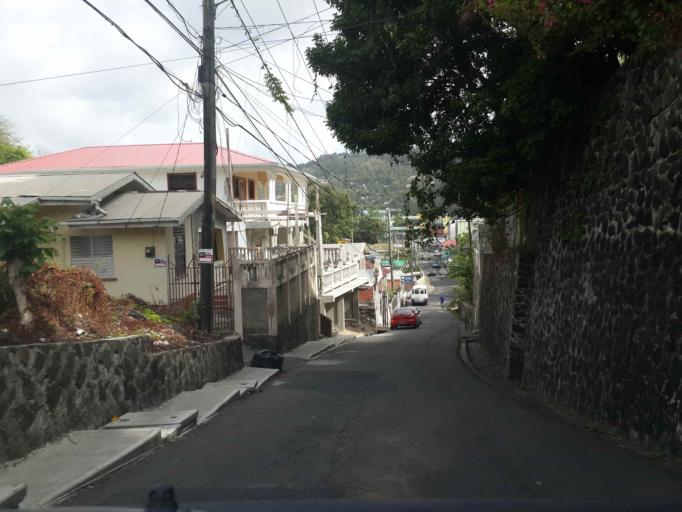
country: LC
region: Castries Quarter
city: Bisee
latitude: 14.0146
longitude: -60.9877
